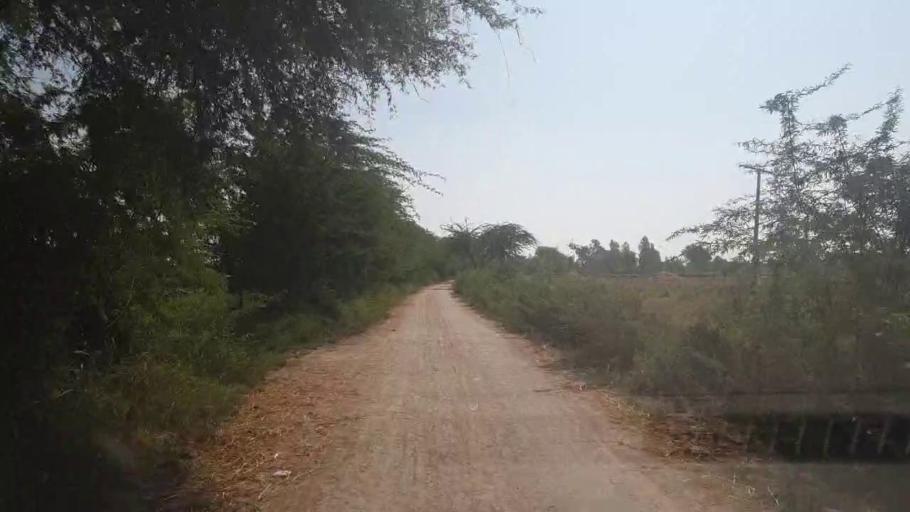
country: PK
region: Sindh
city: Badin
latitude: 24.6335
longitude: 68.9126
